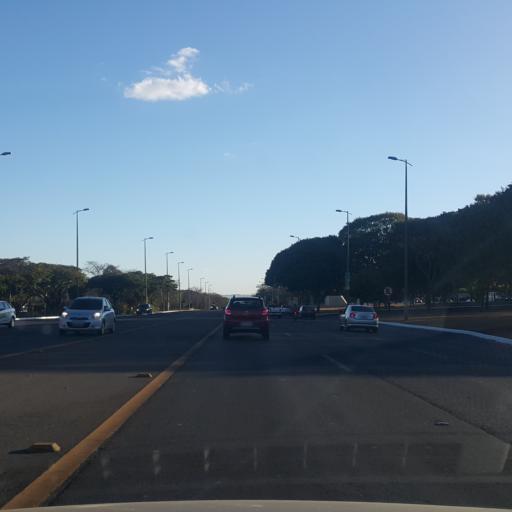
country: BR
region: Federal District
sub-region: Brasilia
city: Brasilia
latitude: -15.8176
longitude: -47.9016
